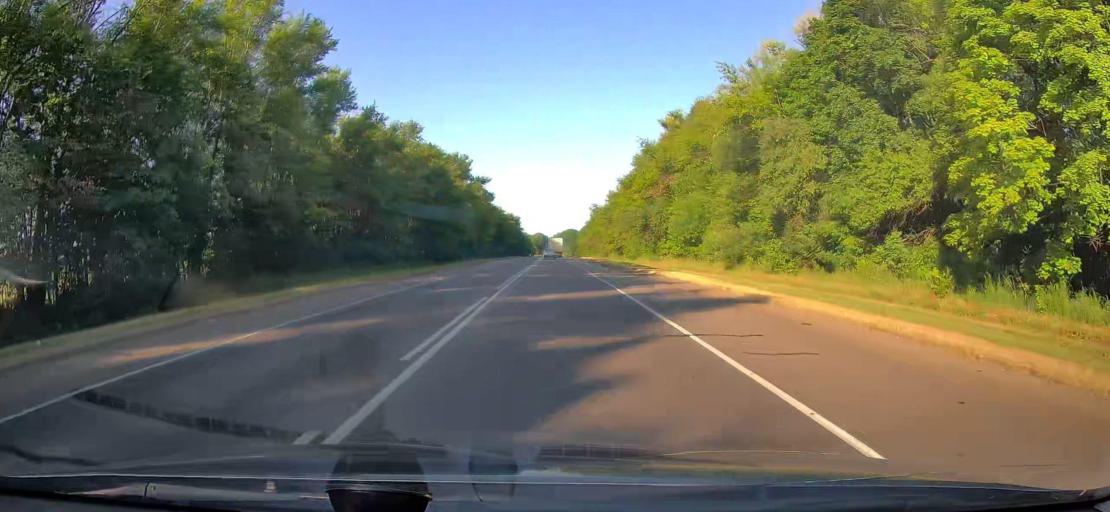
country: RU
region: Tula
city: Chern'
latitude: 53.4731
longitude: 36.9708
